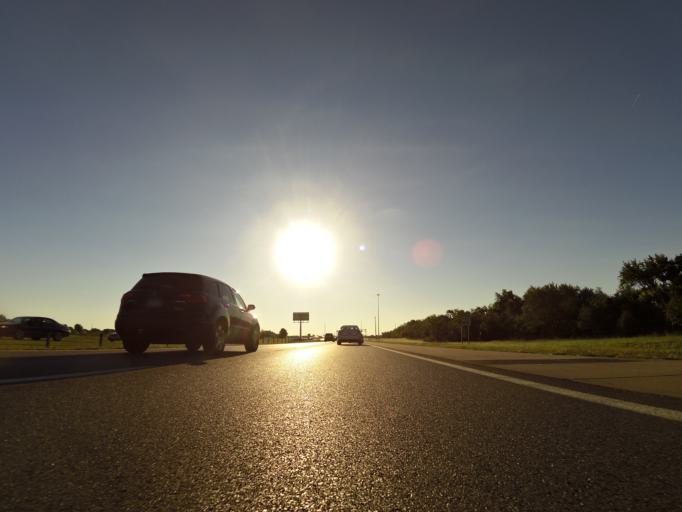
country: US
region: Kansas
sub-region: Sedgwick County
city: Bellaire
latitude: 37.7454
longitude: -97.2692
